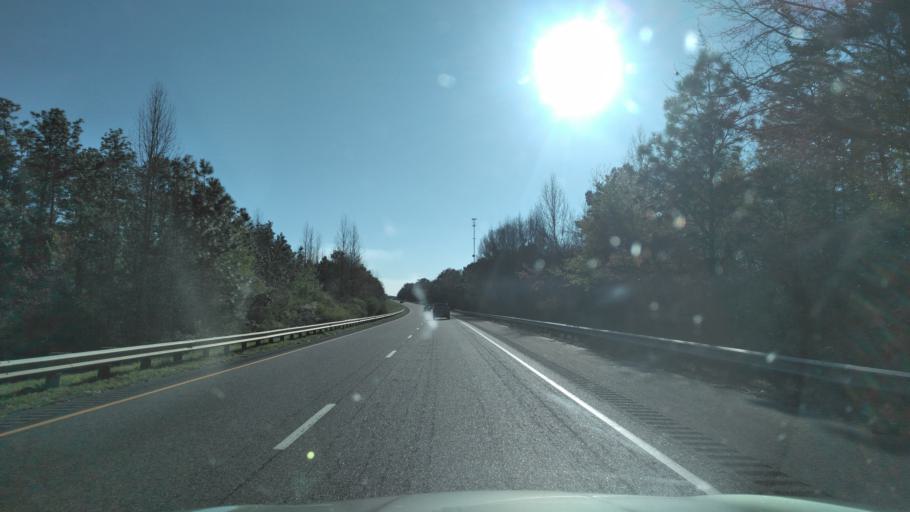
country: US
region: Alabama
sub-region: Escambia County
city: Atmore
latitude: 31.0592
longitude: -87.5808
